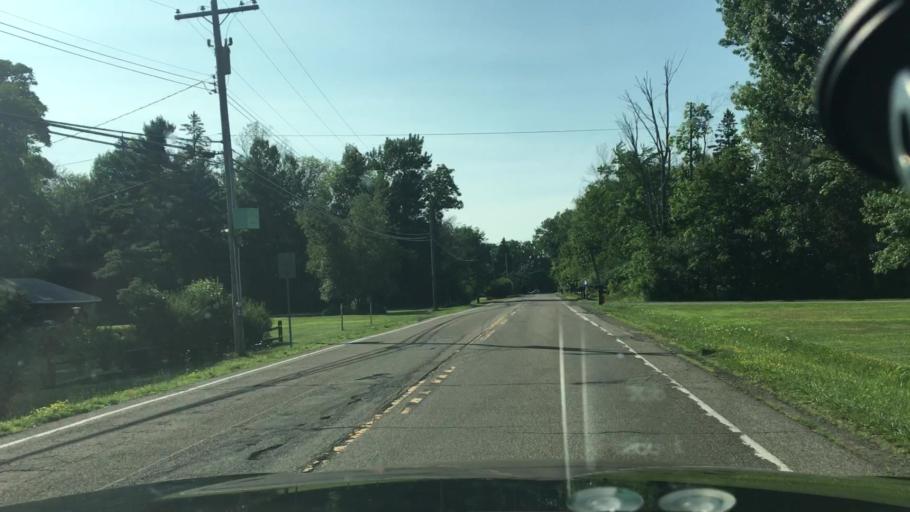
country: US
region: New York
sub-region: Erie County
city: Angola on the Lake
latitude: 42.6411
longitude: -79.0587
